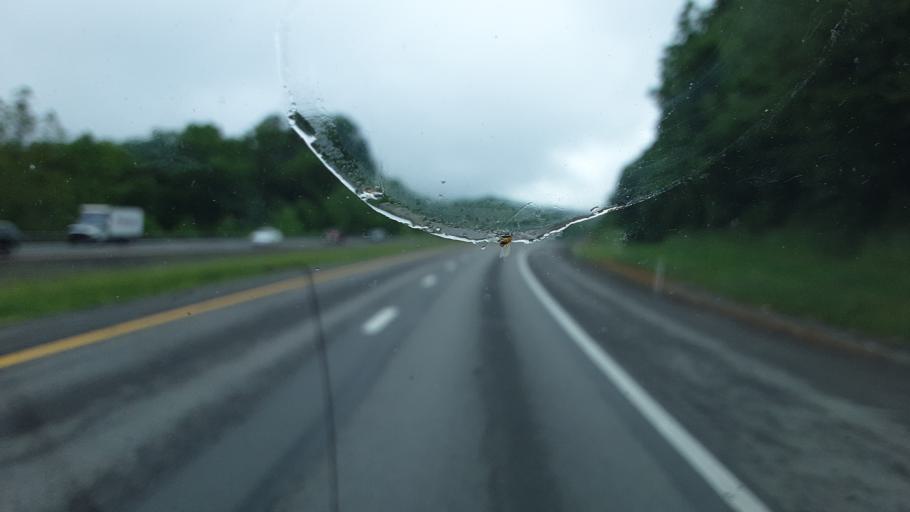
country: US
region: West Virginia
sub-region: Fayette County
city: Oak Hill
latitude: 37.9583
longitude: -81.2620
